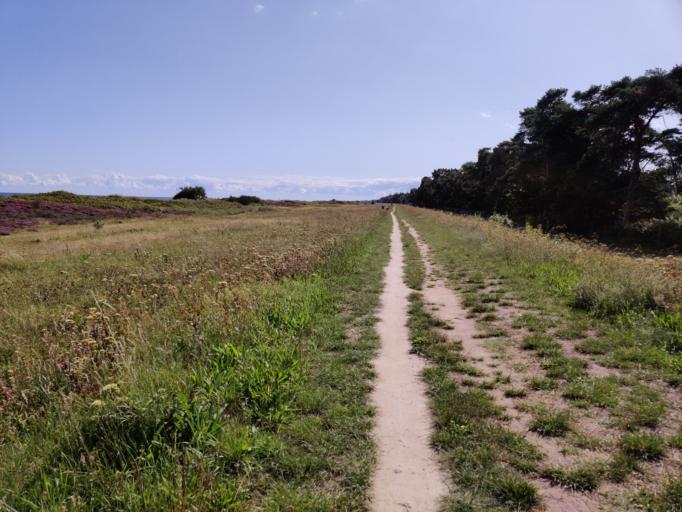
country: DK
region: Zealand
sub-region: Guldborgsund Kommune
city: Nykobing Falster
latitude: 54.6545
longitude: 11.9597
